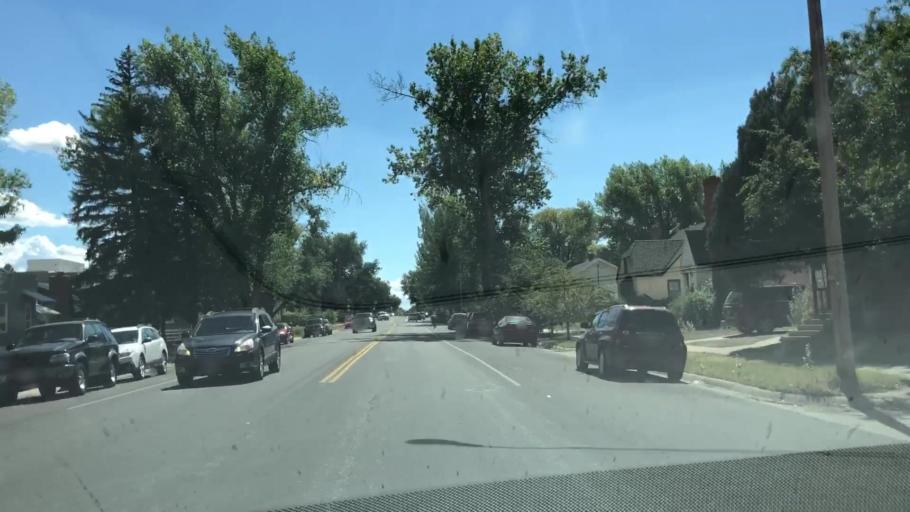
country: US
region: Wyoming
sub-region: Albany County
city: Laramie
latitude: 41.3171
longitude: -105.5851
